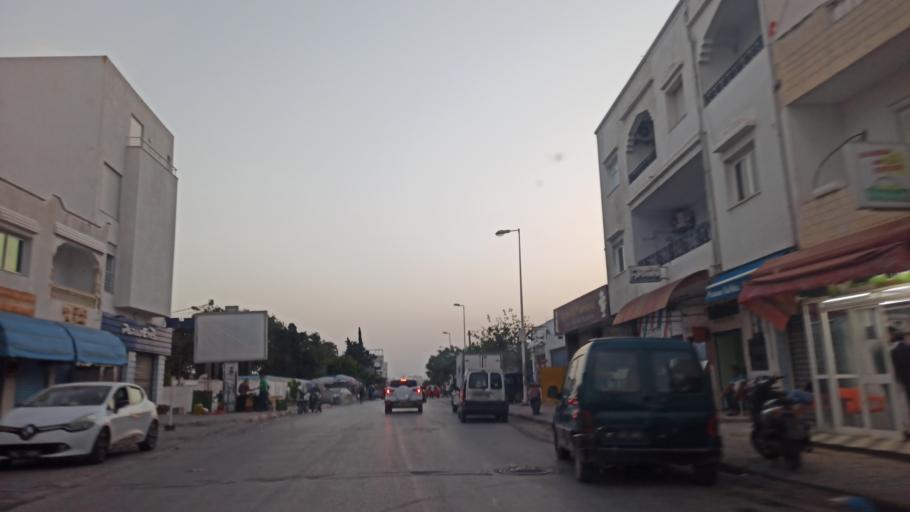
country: TN
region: Nabul
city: Al Hammamat
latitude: 36.4059
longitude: 10.6169
